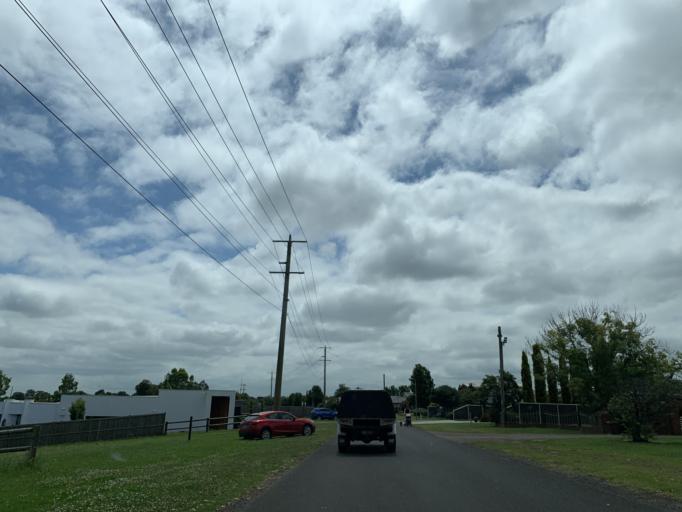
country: AU
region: Victoria
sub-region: Wellington
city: Sale
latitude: -38.1209
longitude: 147.0902
